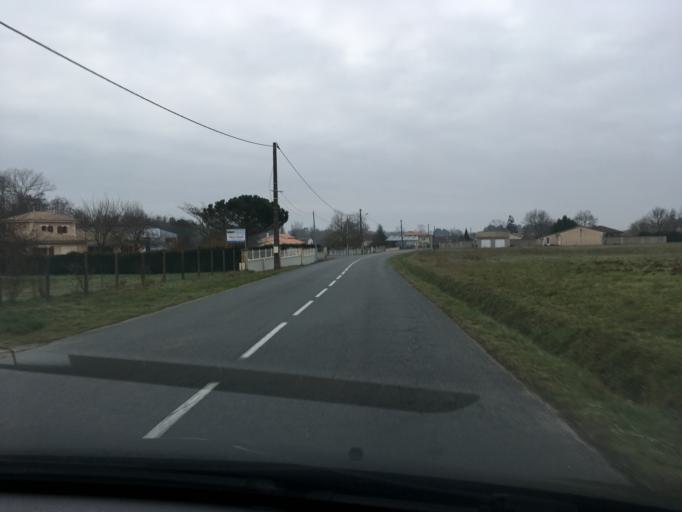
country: FR
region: Aquitaine
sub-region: Departement de la Gironde
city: Saint-Ciers-sur-Gironde
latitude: 45.2831
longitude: -0.6015
